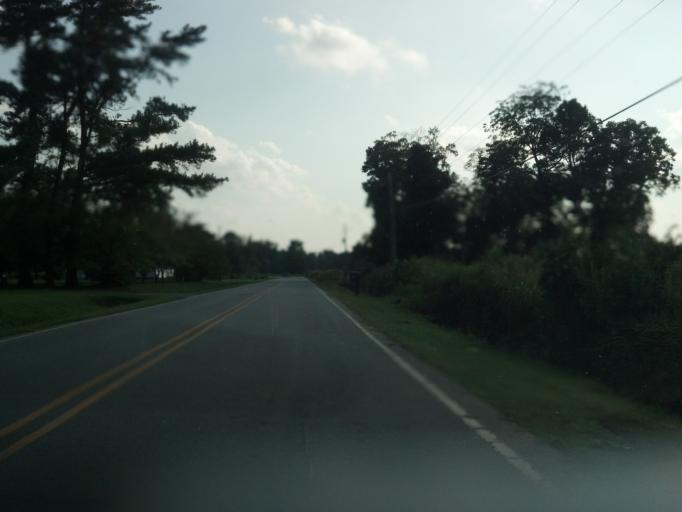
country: US
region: North Carolina
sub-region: Pitt County
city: Winterville
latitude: 35.5067
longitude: -77.4146
